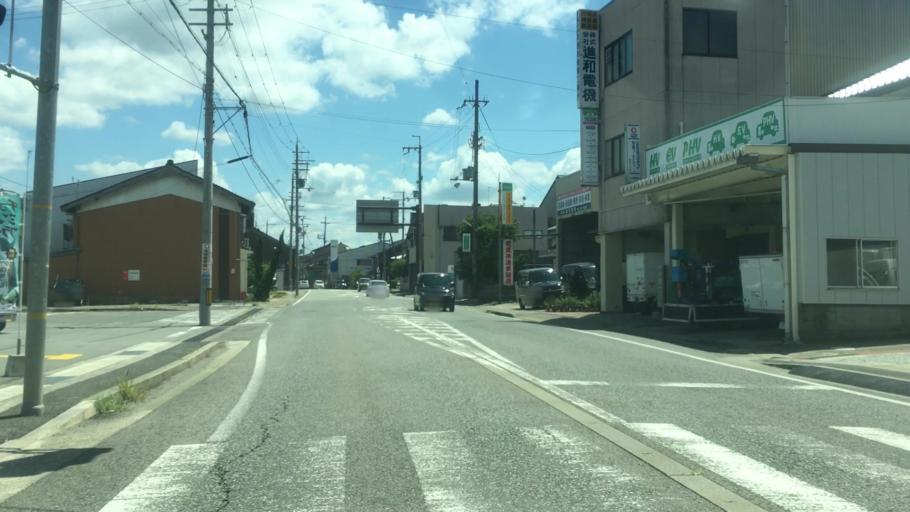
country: JP
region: Hyogo
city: Toyooka
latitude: 35.5401
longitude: 134.8241
